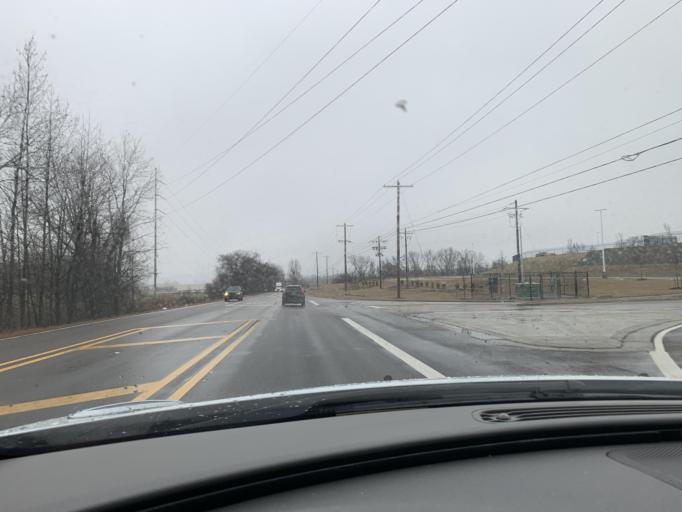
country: US
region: Mississippi
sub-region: De Soto County
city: Horn Lake
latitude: 34.9092
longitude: -89.9998
